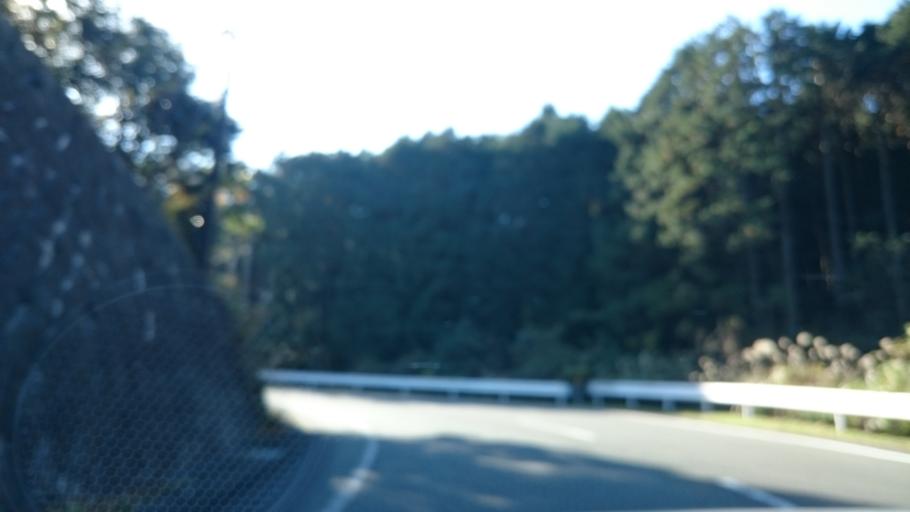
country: JP
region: Shizuoka
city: Heda
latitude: 34.9955
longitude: 138.8138
